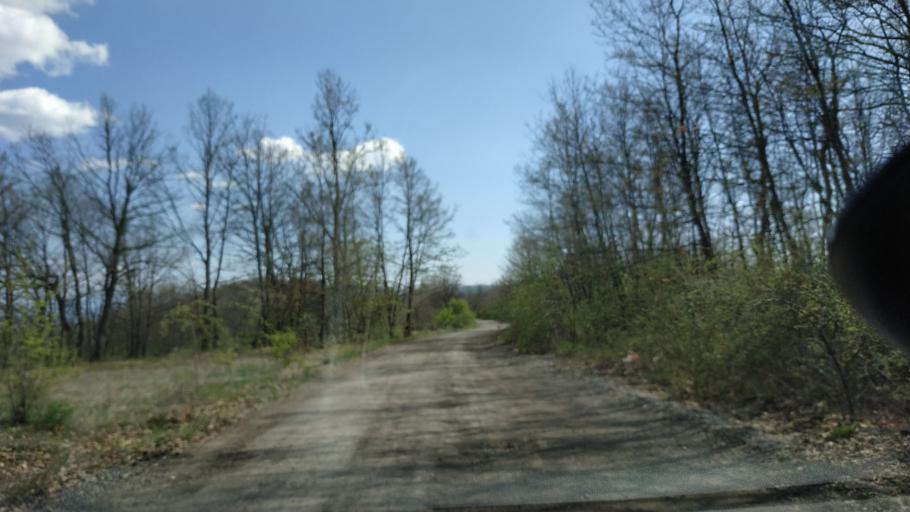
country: RS
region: Central Serbia
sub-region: Zajecarski Okrug
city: Soko Banja
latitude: 43.5347
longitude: 21.9061
